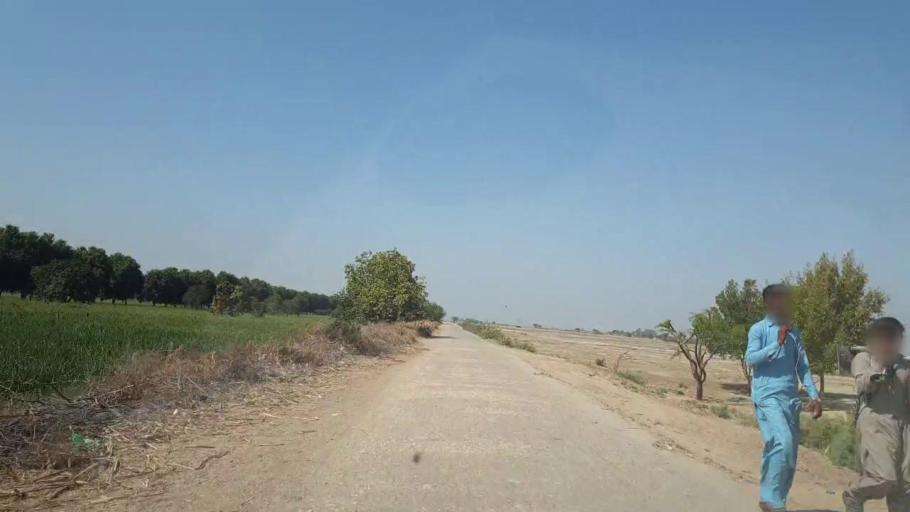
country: PK
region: Sindh
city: Mirpur Khas
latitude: 25.6699
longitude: 69.1113
